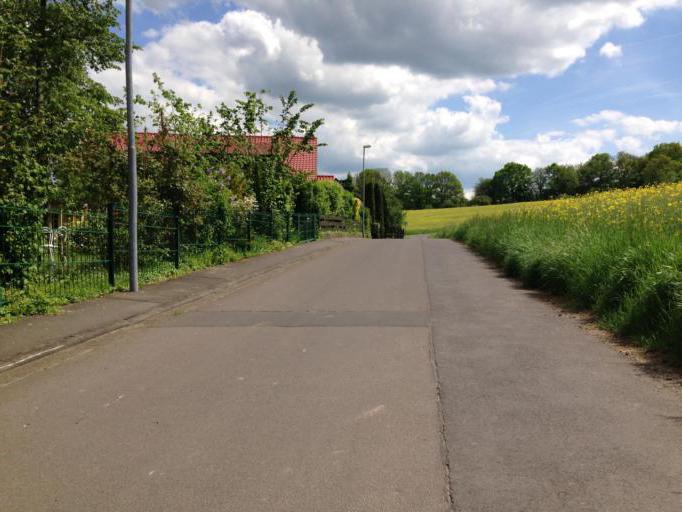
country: DE
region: Hesse
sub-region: Regierungsbezirk Giessen
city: Fronhausen
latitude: 50.6736
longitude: 8.6932
